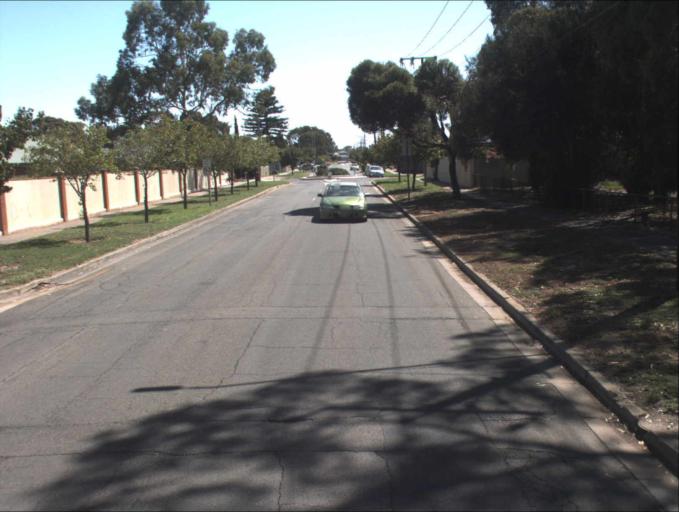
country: AU
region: South Australia
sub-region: Port Adelaide Enfield
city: Klemzig
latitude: -34.8709
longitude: 138.6246
